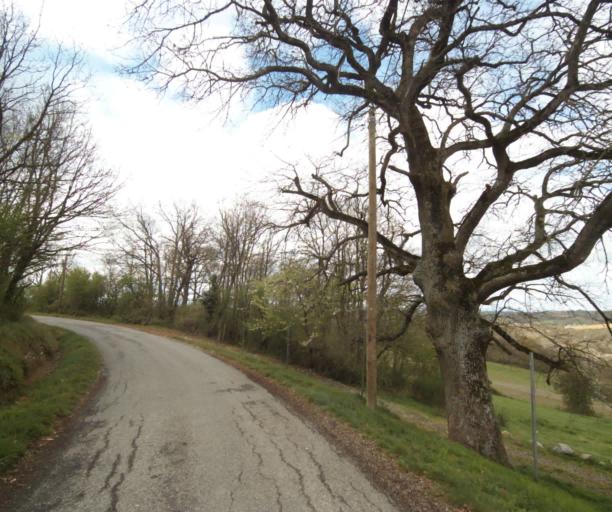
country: FR
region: Midi-Pyrenees
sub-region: Departement de l'Ariege
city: Saverdun
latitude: 43.2138
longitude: 1.5395
